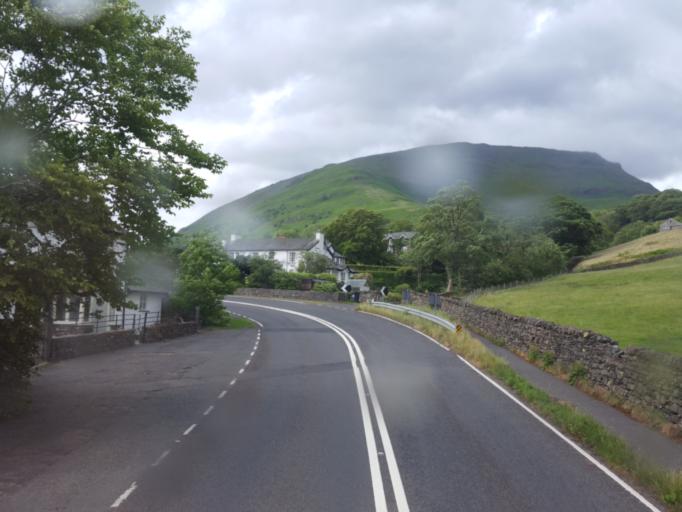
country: GB
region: England
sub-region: Cumbria
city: Ambleside
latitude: 54.4726
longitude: -3.0256
